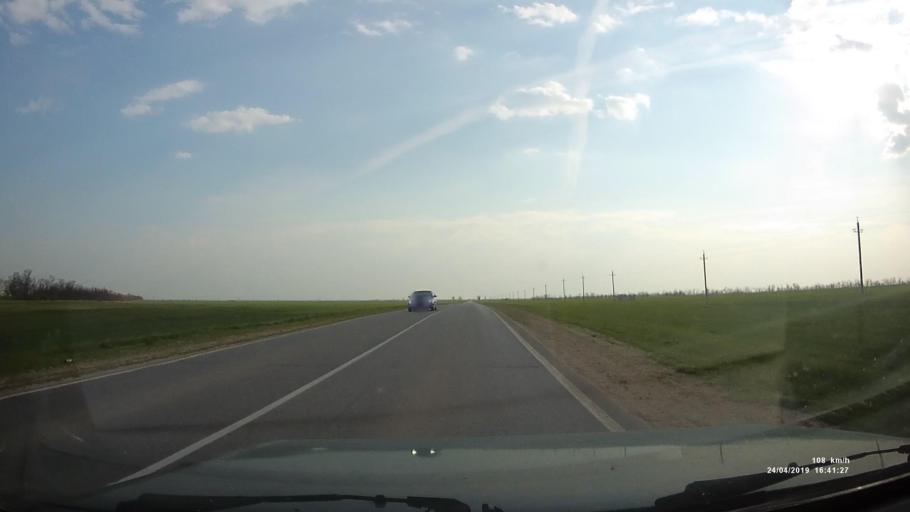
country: RU
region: Rostov
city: Gundorovskiy
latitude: 46.8197
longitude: 41.8671
